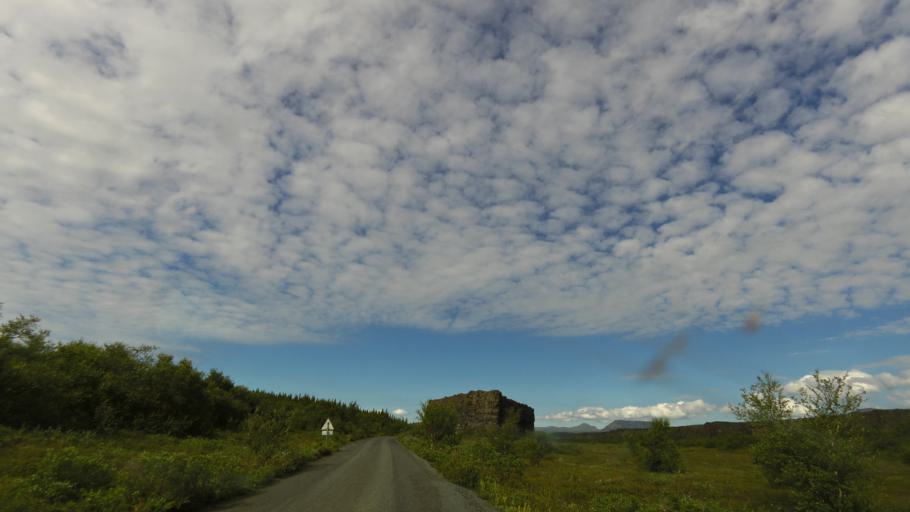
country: IS
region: Northeast
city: Husavik
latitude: 66.0078
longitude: -16.5081
